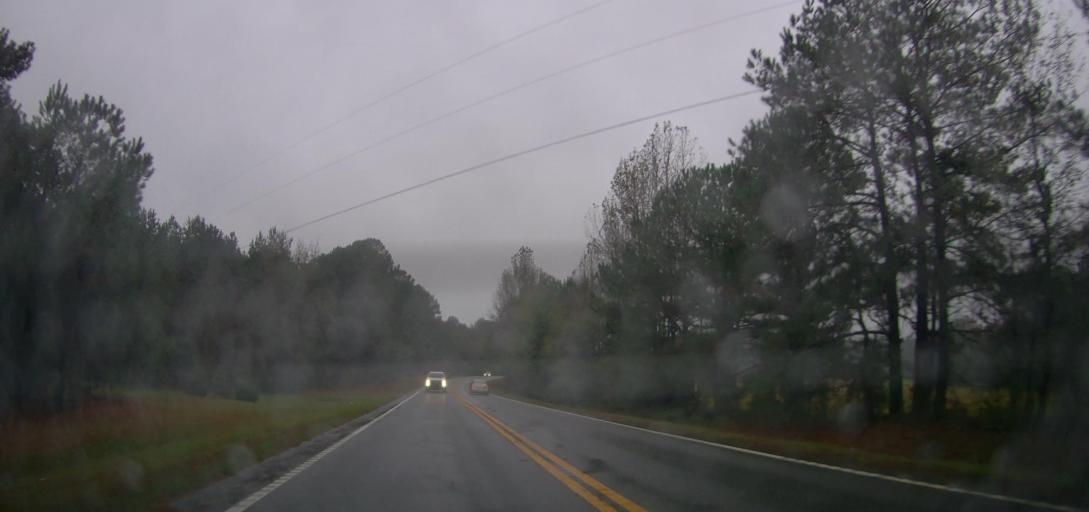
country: US
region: Georgia
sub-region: Jones County
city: Gray
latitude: 33.0318
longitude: -83.5177
